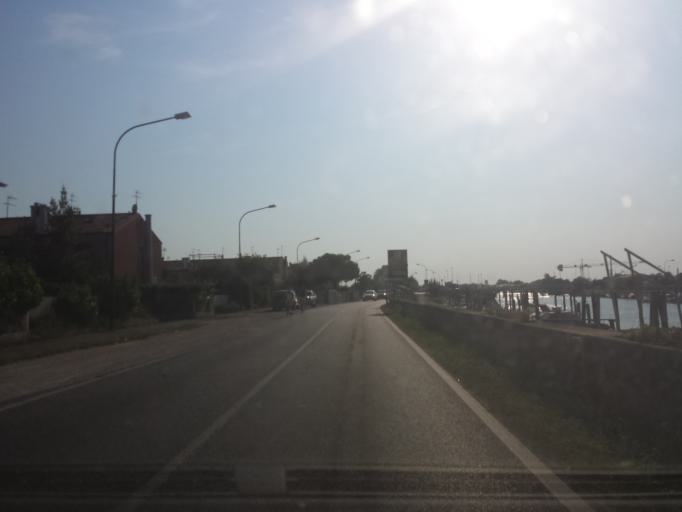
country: IT
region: Veneto
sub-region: Provincia di Venezia
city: Ca' Savio
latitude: 45.4576
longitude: 12.4593
